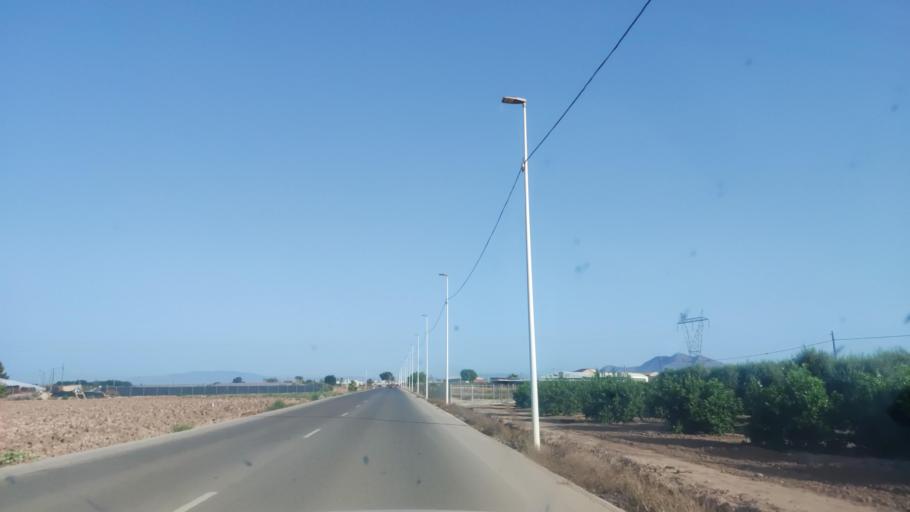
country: ES
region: Murcia
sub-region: Murcia
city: Los Alcazares
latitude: 37.7575
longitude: -0.8649
